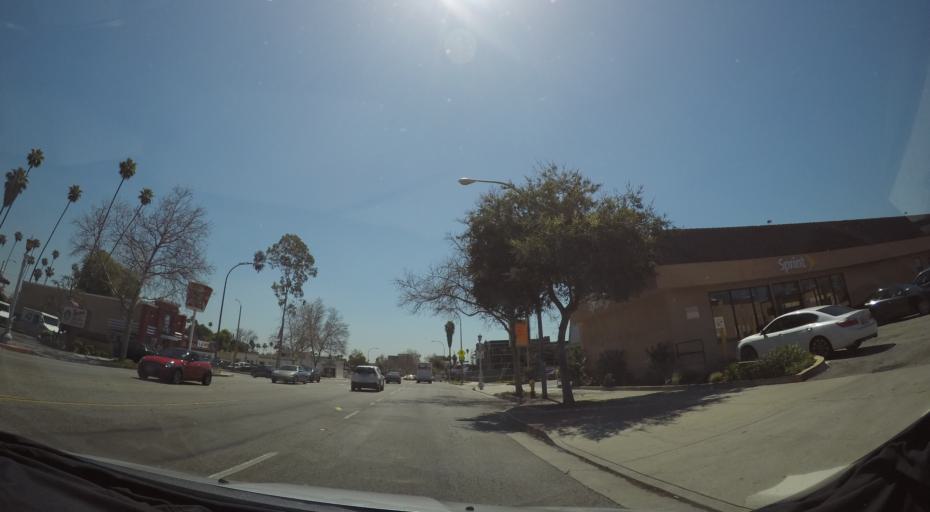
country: US
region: California
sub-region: Los Angeles County
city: Pasadena
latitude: 34.1603
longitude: -118.1326
